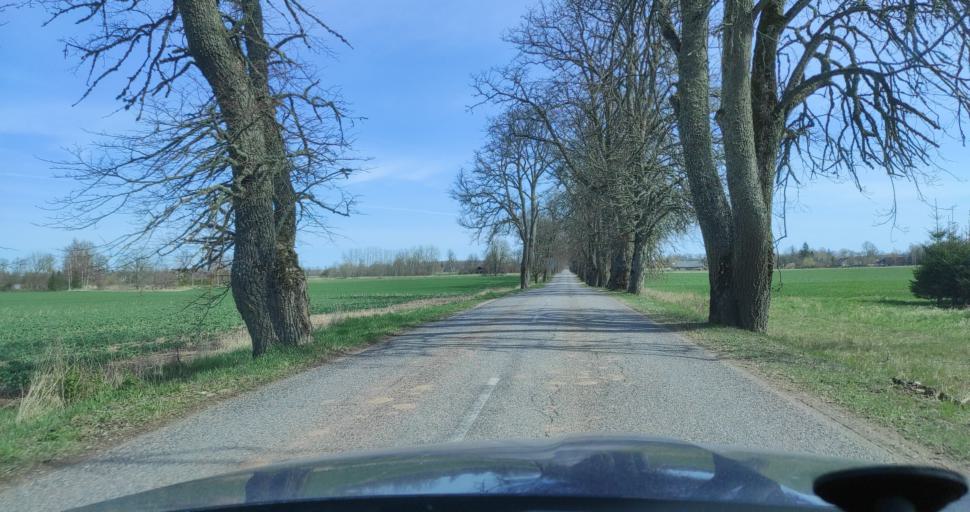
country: LV
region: Talsu Rajons
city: Stende
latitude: 57.2177
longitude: 22.5035
